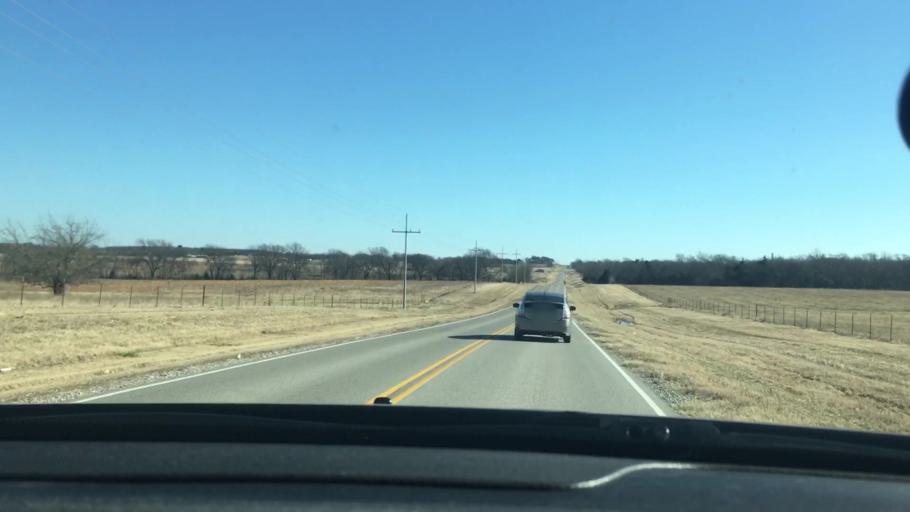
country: US
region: Oklahoma
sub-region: Murray County
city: Davis
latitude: 34.4772
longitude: -97.0768
